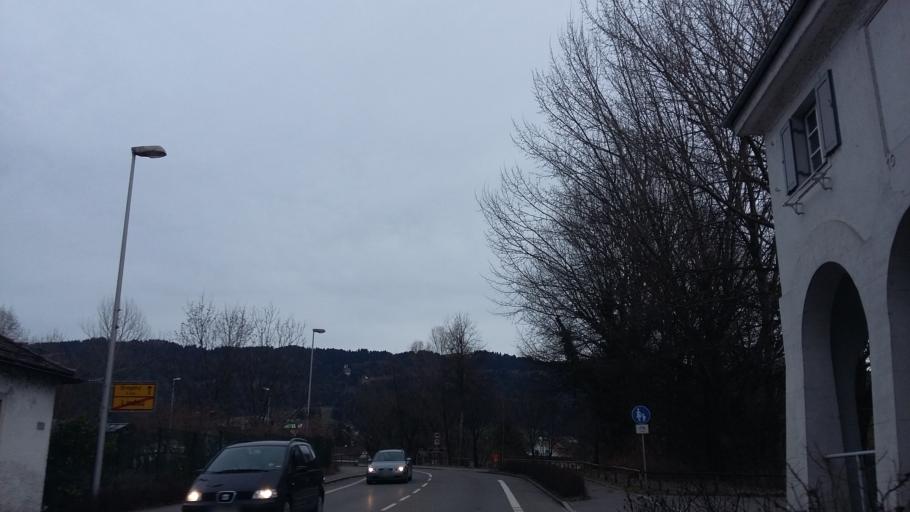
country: AT
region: Vorarlberg
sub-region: Politischer Bezirk Bregenz
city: Lochau
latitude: 47.5372
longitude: 9.7355
